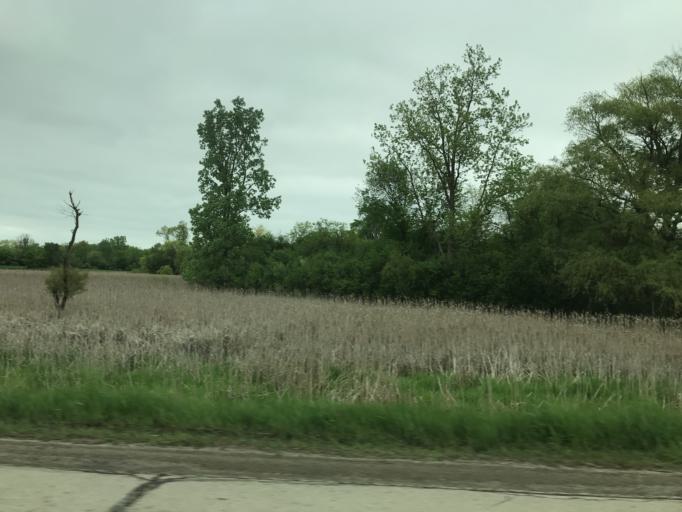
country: US
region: Michigan
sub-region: Washtenaw County
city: Ann Arbor
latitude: 42.2335
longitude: -83.7021
